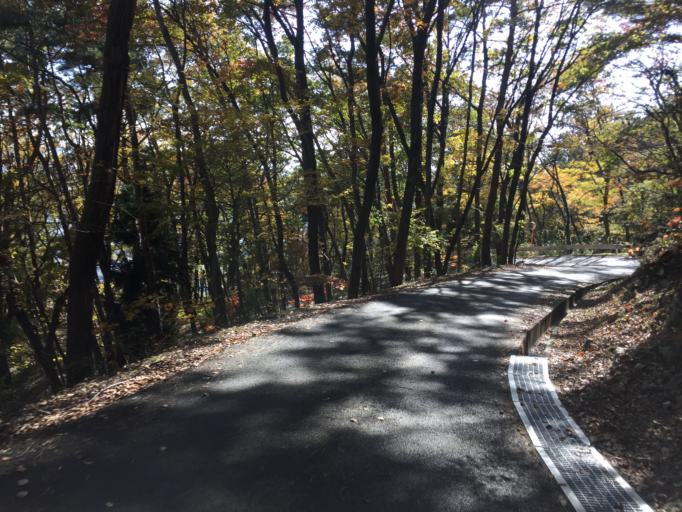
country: JP
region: Fukushima
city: Fukushima-shi
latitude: 37.7702
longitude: 140.4641
